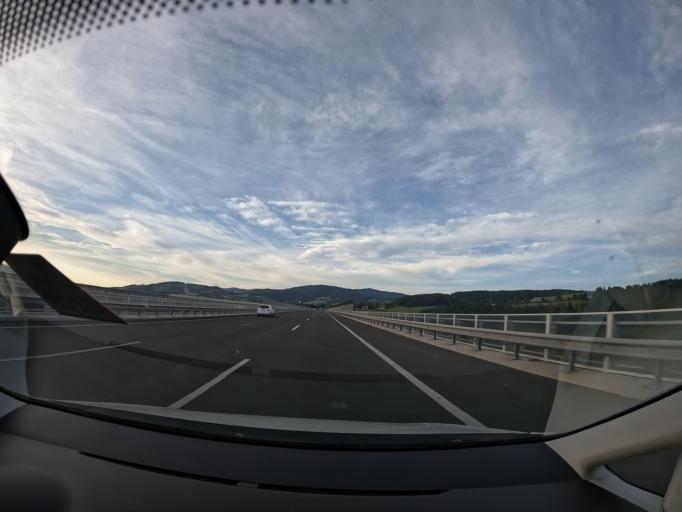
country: AT
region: Carinthia
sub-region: Politischer Bezirk Wolfsberg
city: Bad Sankt Leonhard im Lavanttal
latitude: 46.9258
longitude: 14.8229
